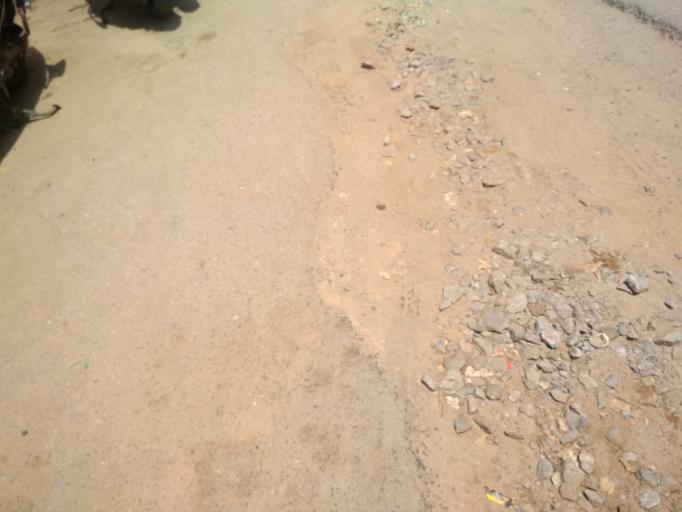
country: IN
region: Karnataka
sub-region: Bangalore Urban
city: Bangalore
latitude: 12.9319
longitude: 77.6840
